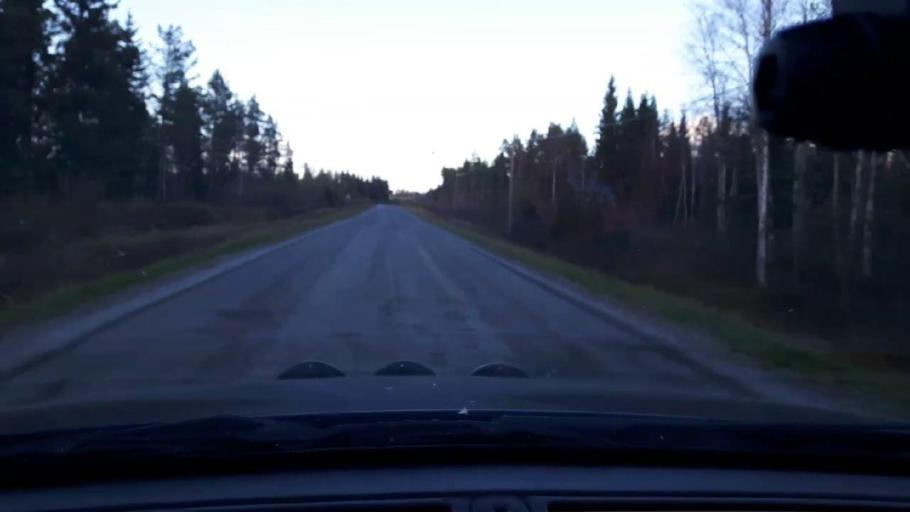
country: SE
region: Jaemtland
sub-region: Bergs Kommun
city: Hoverberg
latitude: 63.0691
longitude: 14.2673
